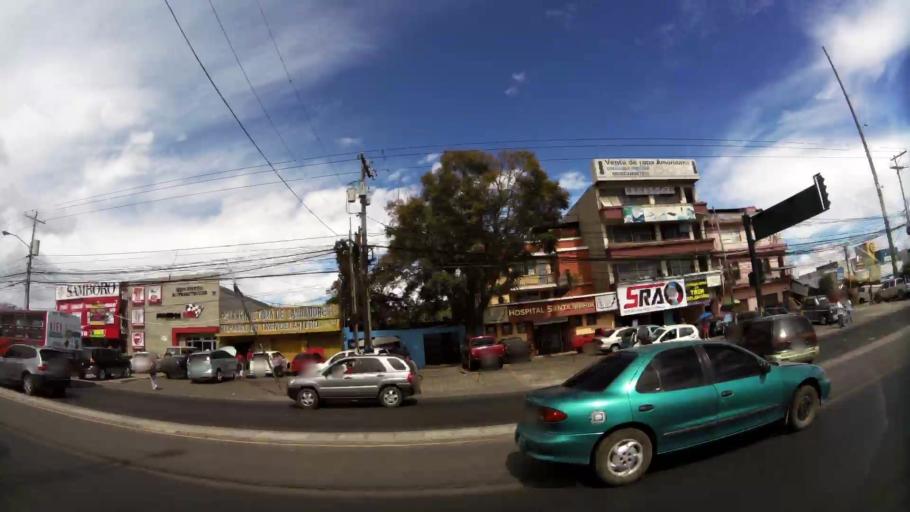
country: GT
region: Guatemala
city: Mixco
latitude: 14.6467
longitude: -90.5796
